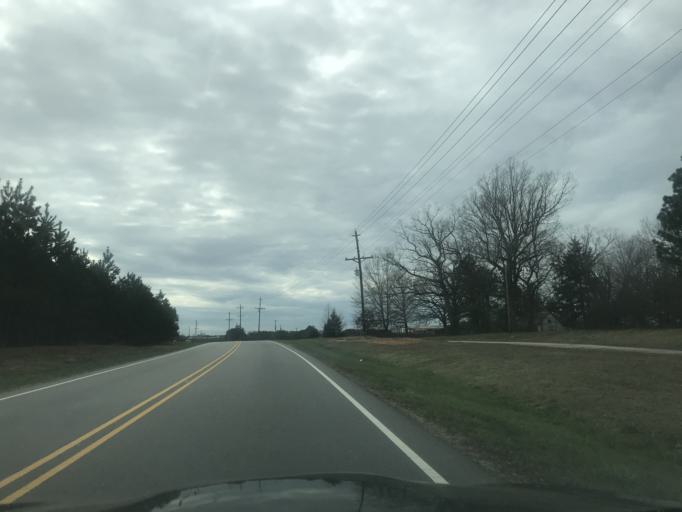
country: US
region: North Carolina
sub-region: Franklin County
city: Louisburg
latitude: 36.0869
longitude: -78.3269
